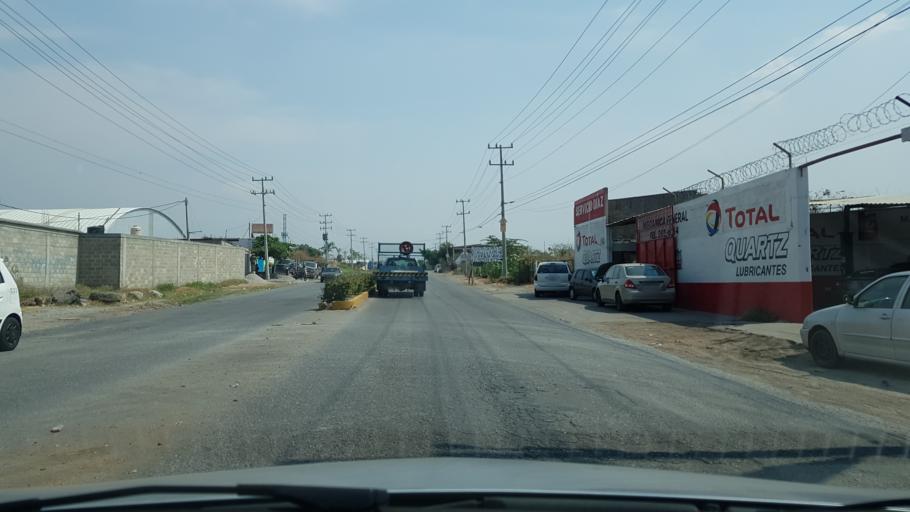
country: MX
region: Morelos
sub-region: Xochitepec
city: Chiconcuac
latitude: 18.7985
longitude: -99.1993
